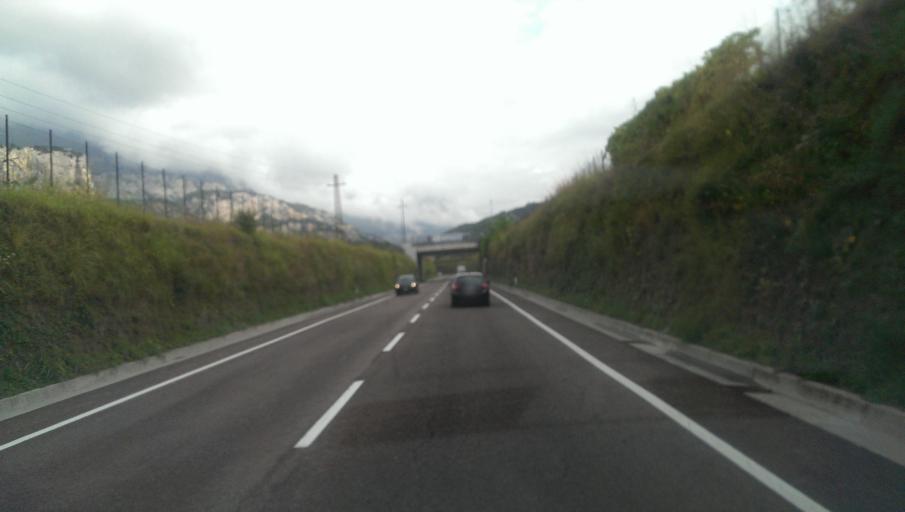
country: IT
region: Trentino-Alto Adige
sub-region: Provincia di Trento
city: Arco
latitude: 45.9175
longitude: 10.8961
